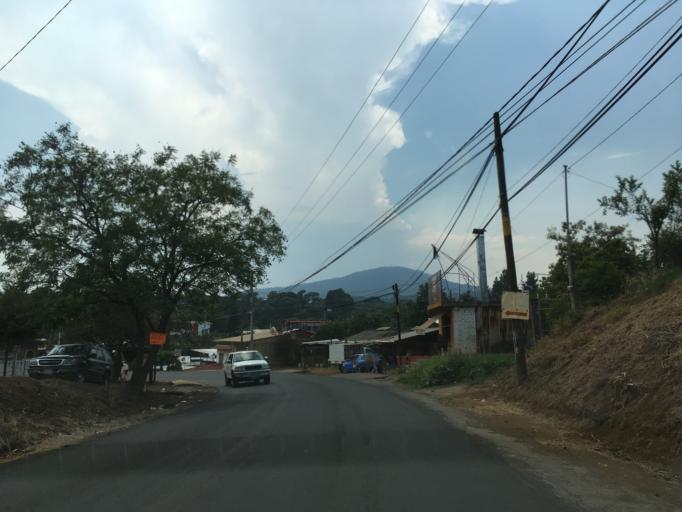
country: MX
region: Michoacan
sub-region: Ziracuaretiro
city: Patuan
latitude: 19.4173
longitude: -101.9168
